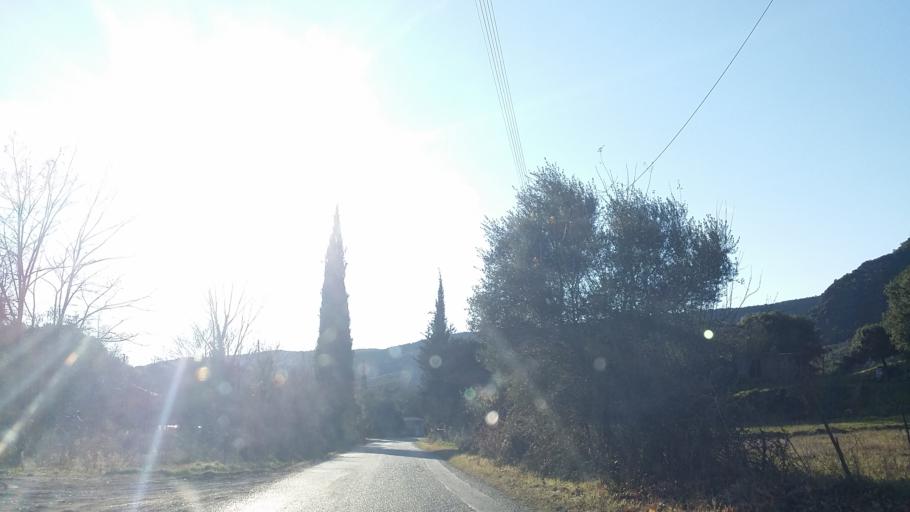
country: GR
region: West Greece
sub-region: Nomos Aitolias kai Akarnanias
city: Neapolis
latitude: 38.7679
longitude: 21.4450
